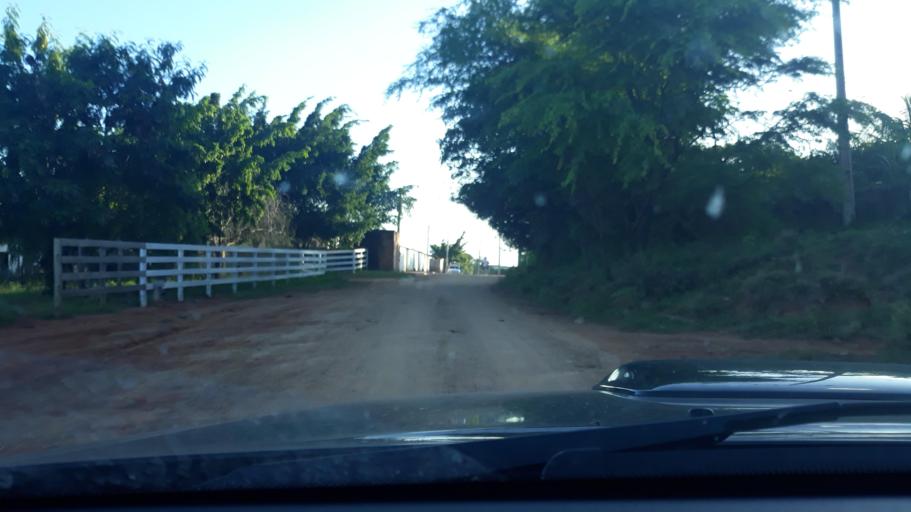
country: BR
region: Bahia
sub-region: Riacho De Santana
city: Riacho de Santana
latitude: -13.8252
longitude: -42.7268
